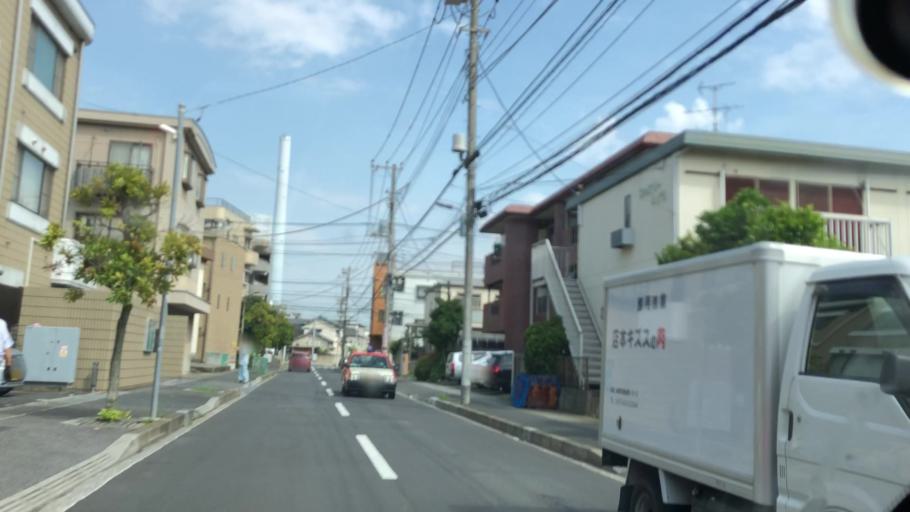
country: JP
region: Tokyo
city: Urayasu
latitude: 35.6805
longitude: 139.9090
